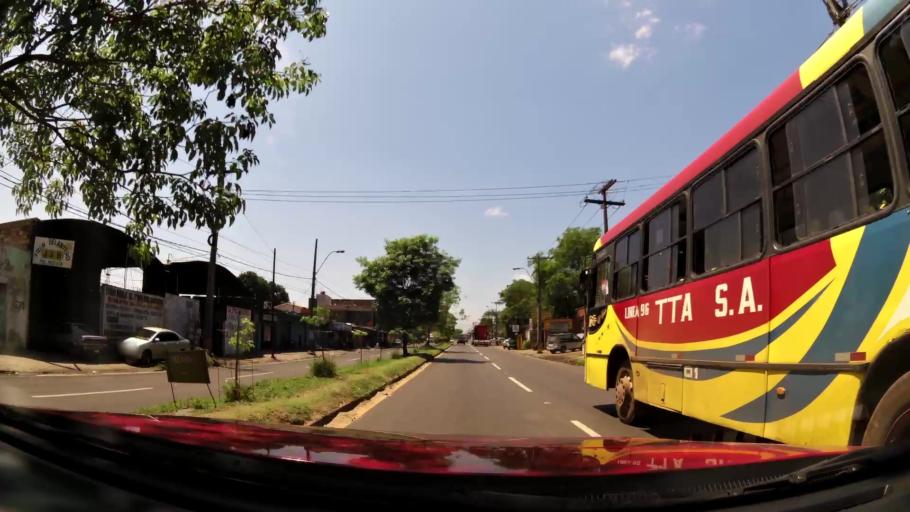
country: PY
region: Central
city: Lambare
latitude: -25.3347
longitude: -57.5791
